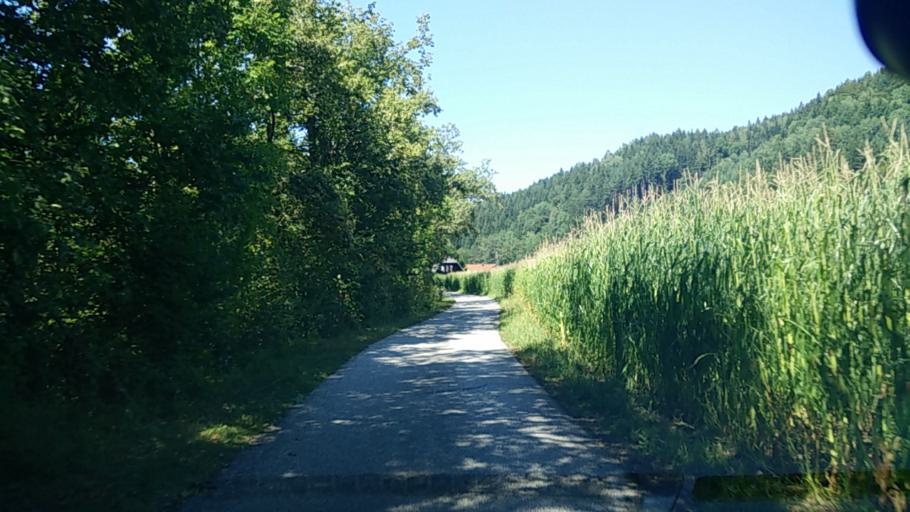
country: AT
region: Carinthia
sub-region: Politischer Bezirk Volkermarkt
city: Sittersdorf
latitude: 46.5451
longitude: 14.5886
